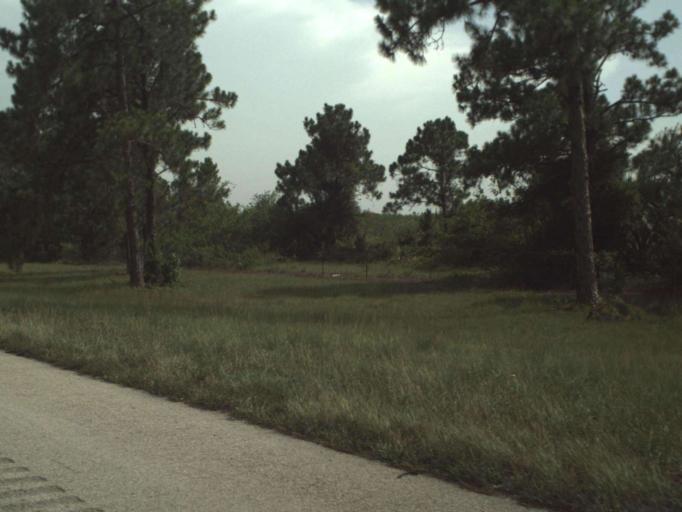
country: US
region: Florida
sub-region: Saint Lucie County
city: Port Saint Lucie
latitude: 27.2241
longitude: -80.4021
